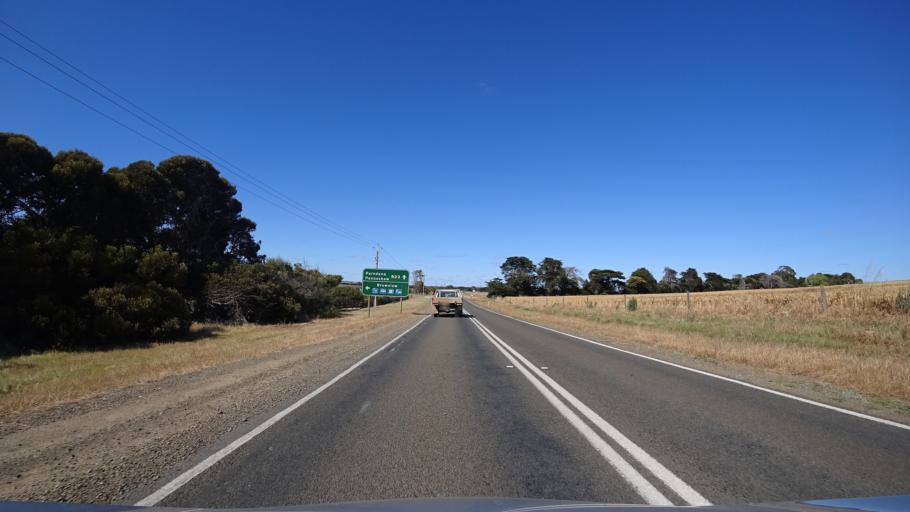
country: AU
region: South Australia
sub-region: Kangaroo Island
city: Kingscote
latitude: -35.6716
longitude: 137.5919
